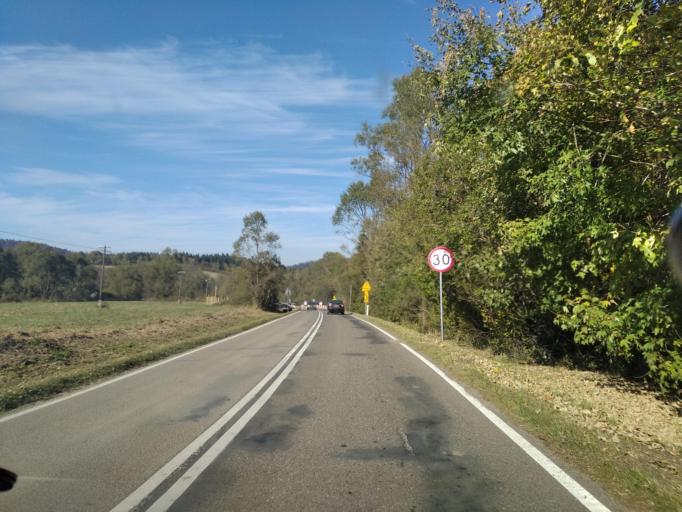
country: PL
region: Subcarpathian Voivodeship
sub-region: Powiat leski
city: Cisna
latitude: 49.2615
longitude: 22.2885
